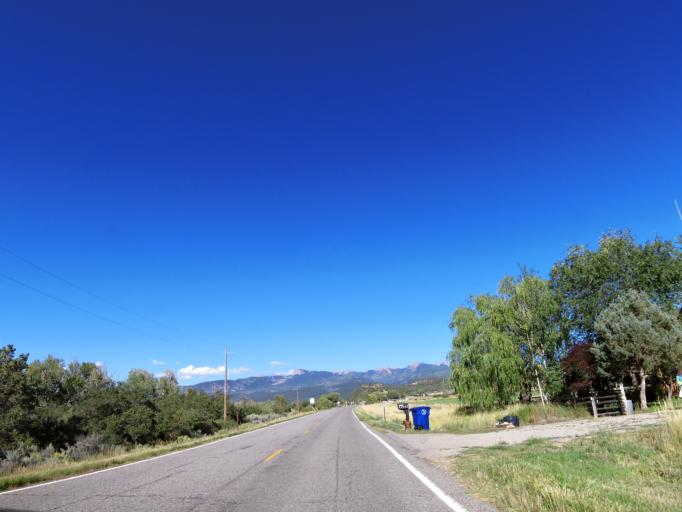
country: US
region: Colorado
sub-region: Montezuma County
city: Mancos
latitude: 37.3465
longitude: -108.2768
